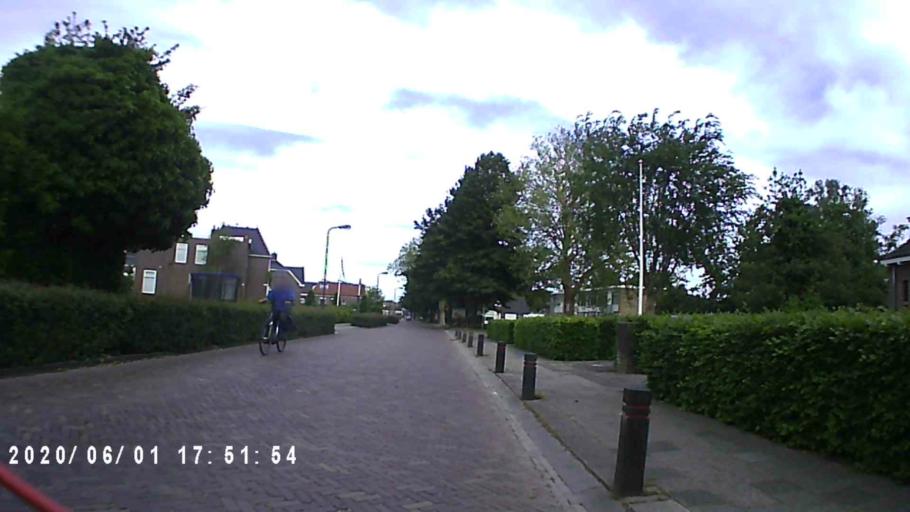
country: NL
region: Friesland
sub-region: Gemeente Tytsjerksteradiel
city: Burgum
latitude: 53.1926
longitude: 5.9849
